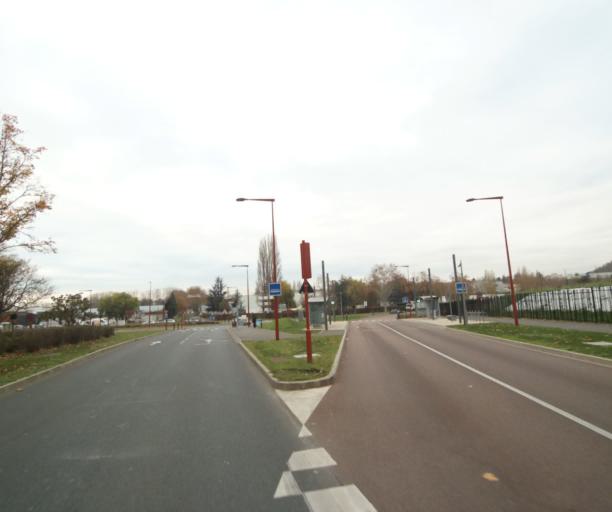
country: FR
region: Ile-de-France
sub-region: Departement du Val-d'Oise
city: Gonesse
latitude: 48.9852
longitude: 2.4607
